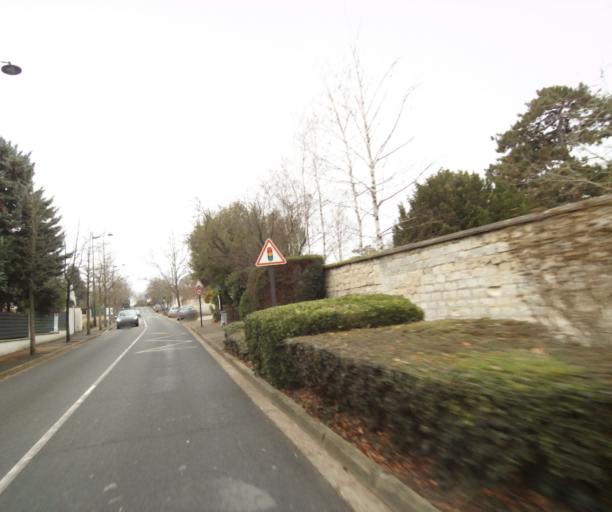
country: FR
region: Ile-de-France
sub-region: Departement des Hauts-de-Seine
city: Rueil-Malmaison
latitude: 48.8670
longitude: 2.1686
